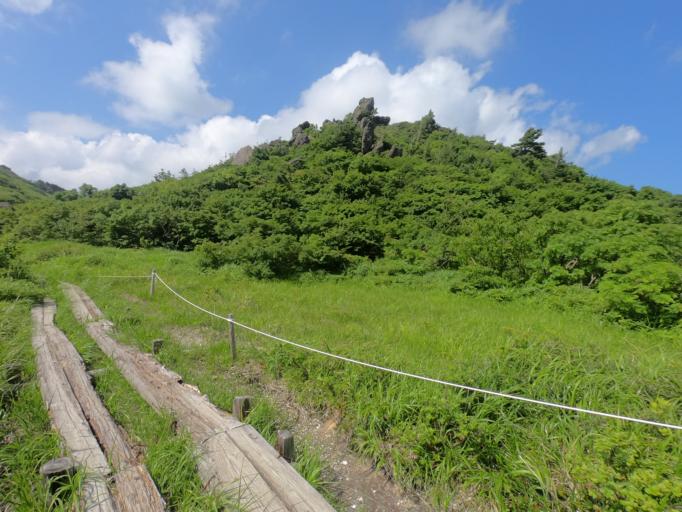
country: JP
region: Akita
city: Yuzawa
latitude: 38.9737
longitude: 140.7754
